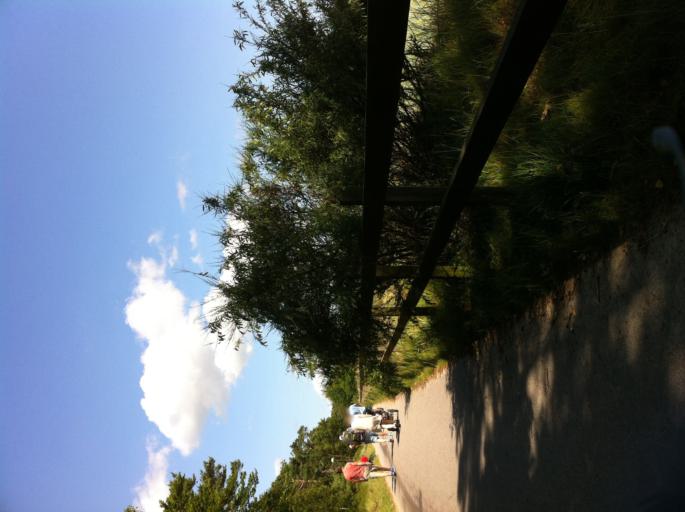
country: SE
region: Skane
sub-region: Ystads Kommun
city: Ystad
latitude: 55.4275
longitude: 13.8547
